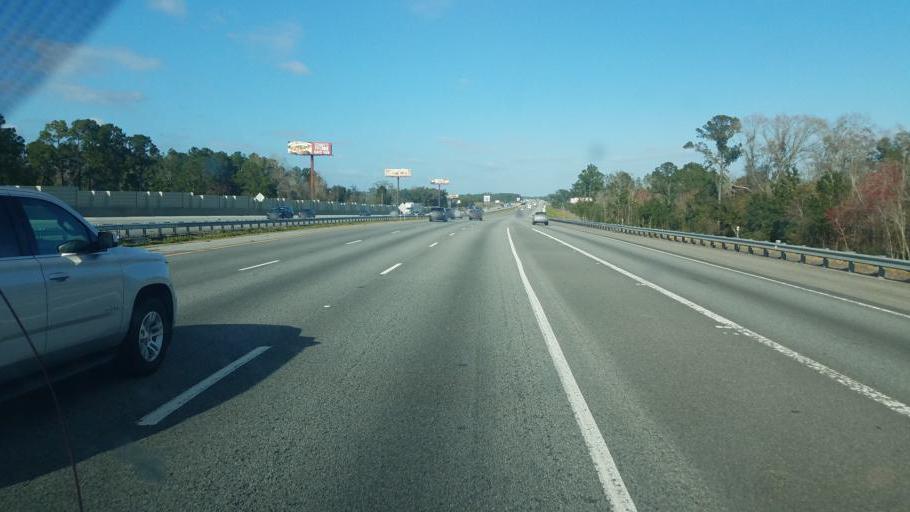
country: US
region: Georgia
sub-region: Glynn County
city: Brunswick
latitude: 31.1422
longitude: -81.5704
